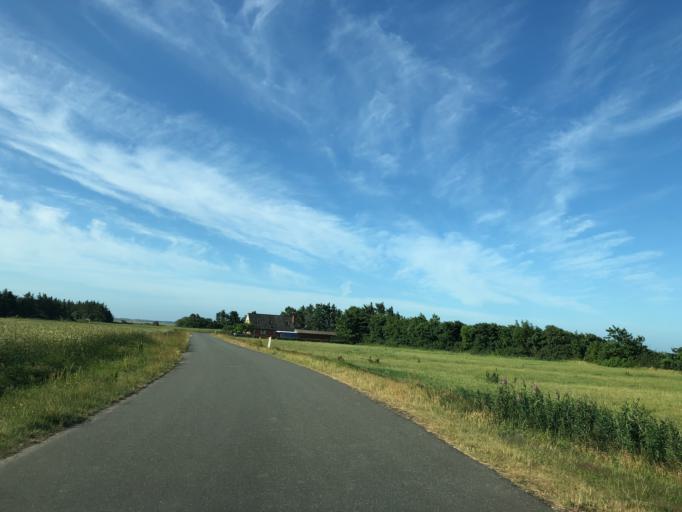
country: DK
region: Central Jutland
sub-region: Holstebro Kommune
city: Ulfborg
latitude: 56.3362
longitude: 8.2713
